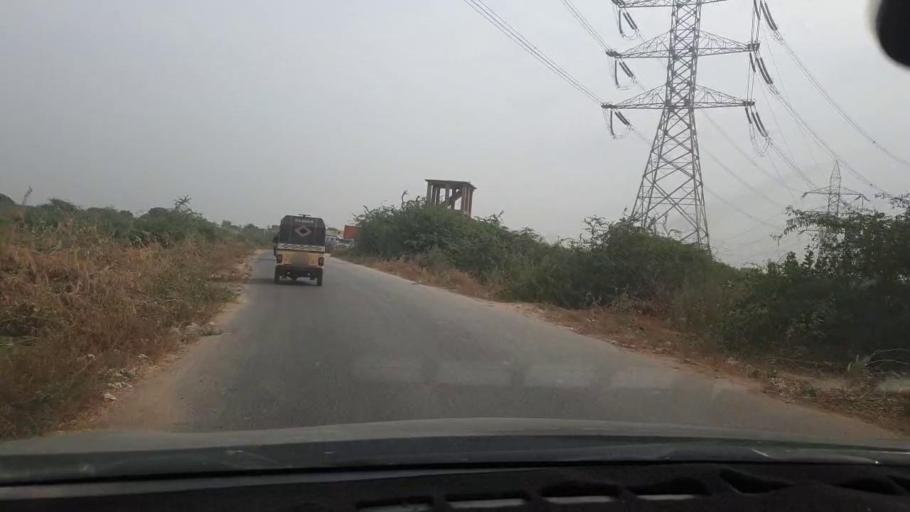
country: PK
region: Sindh
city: Malir Cantonment
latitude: 24.9103
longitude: 67.2845
